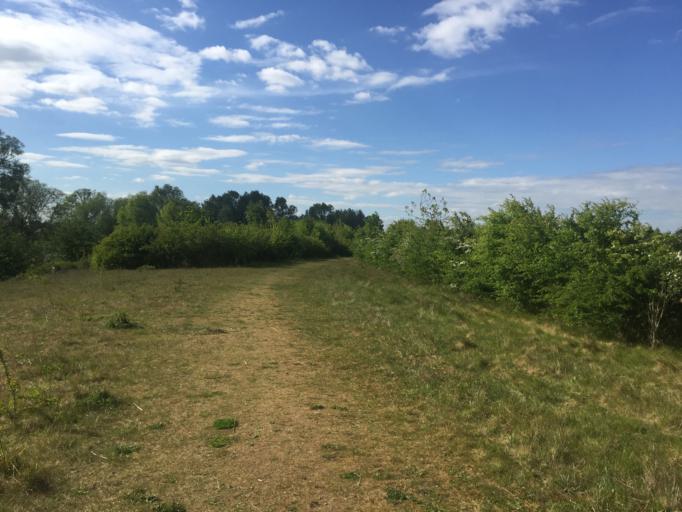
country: GB
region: England
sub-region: Royal Borough of Windsor and Maidenhead
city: Bray
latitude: 51.5070
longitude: -0.6713
